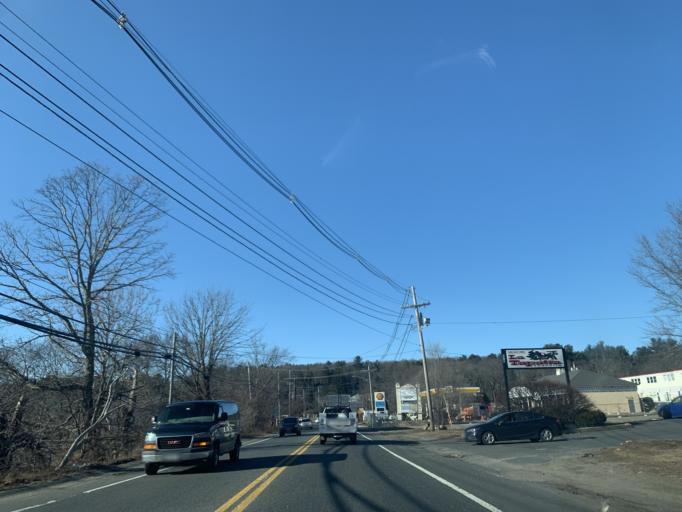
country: US
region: Massachusetts
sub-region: Middlesex County
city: Marlborough
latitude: 42.3484
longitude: -71.5157
